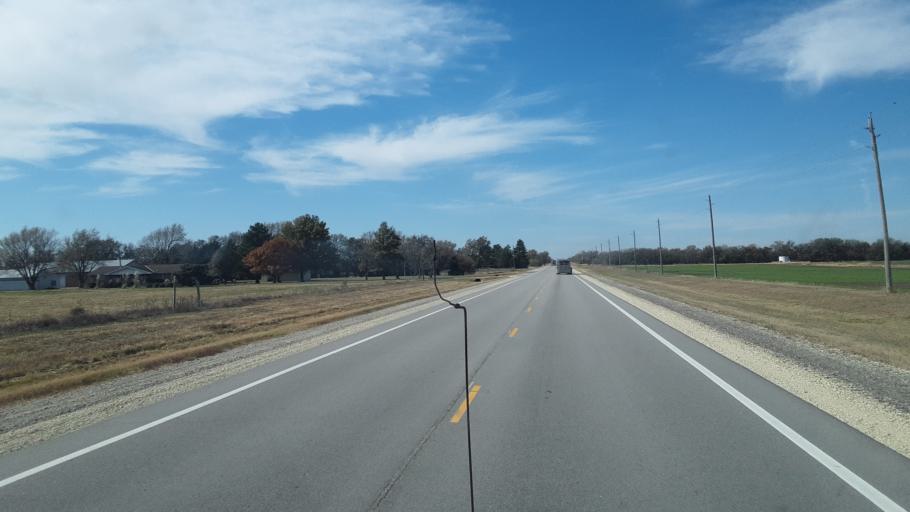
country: US
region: Kansas
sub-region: McPherson County
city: Moundridge
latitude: 38.3767
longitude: -97.4862
